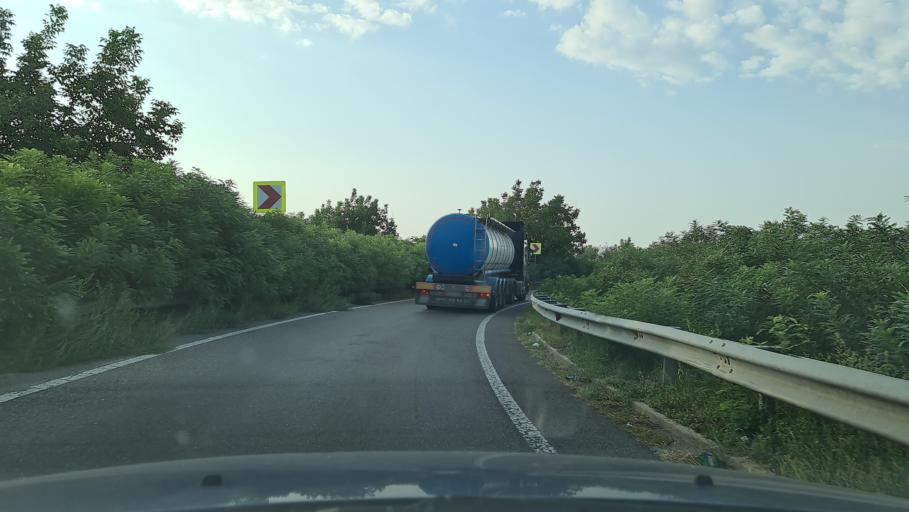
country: RO
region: Calarasi
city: Lehliu-Gara
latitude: 44.4255
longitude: 26.8640
